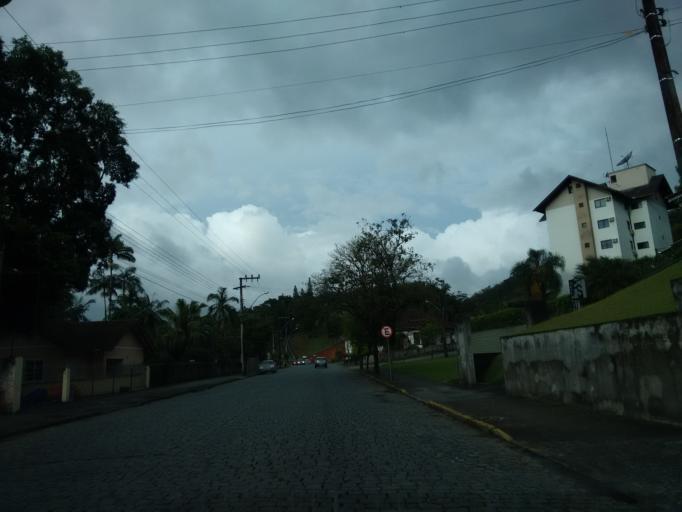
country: BR
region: Santa Catarina
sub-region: Pomerode
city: Pomerode
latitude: -26.7320
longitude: -49.1728
